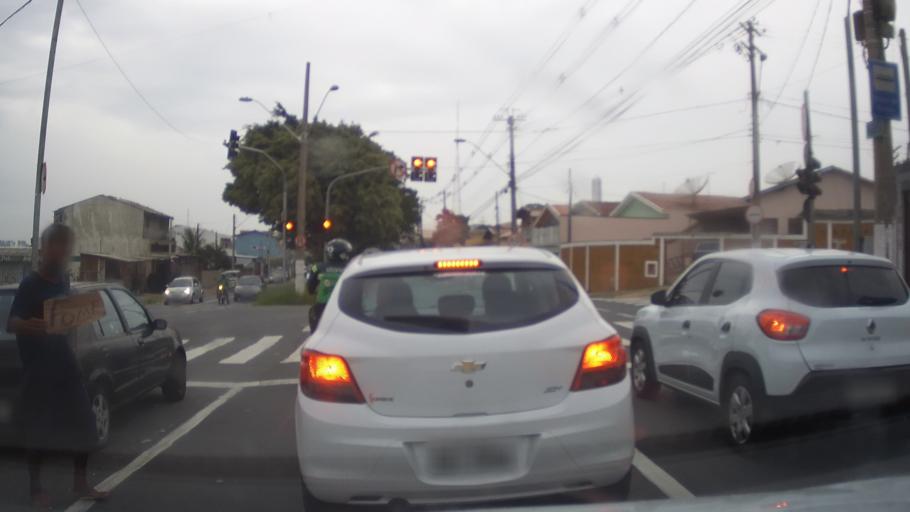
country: BR
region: Sao Paulo
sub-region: Campinas
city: Campinas
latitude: -22.9288
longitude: -47.0323
